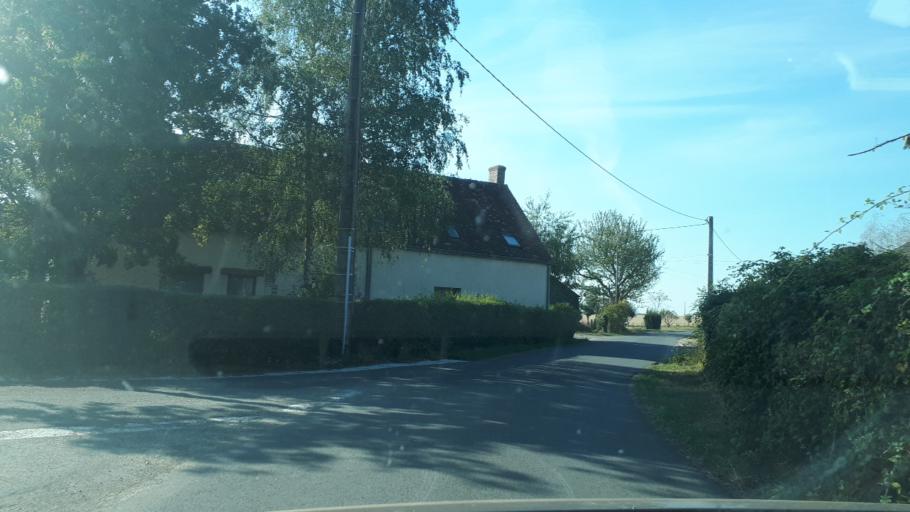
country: FR
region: Centre
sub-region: Departement du Loir-et-Cher
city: Lunay
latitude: 47.8359
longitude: 0.9535
